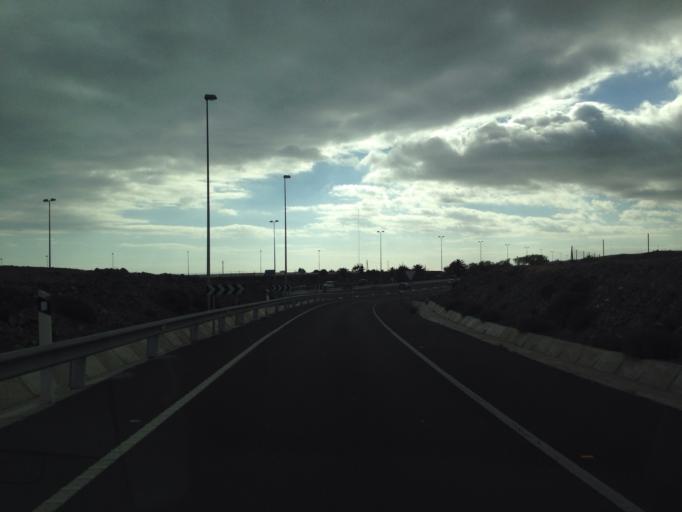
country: ES
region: Canary Islands
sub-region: Provincia de Las Palmas
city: Cruce de Arinaga
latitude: 27.8243
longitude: -15.4586
